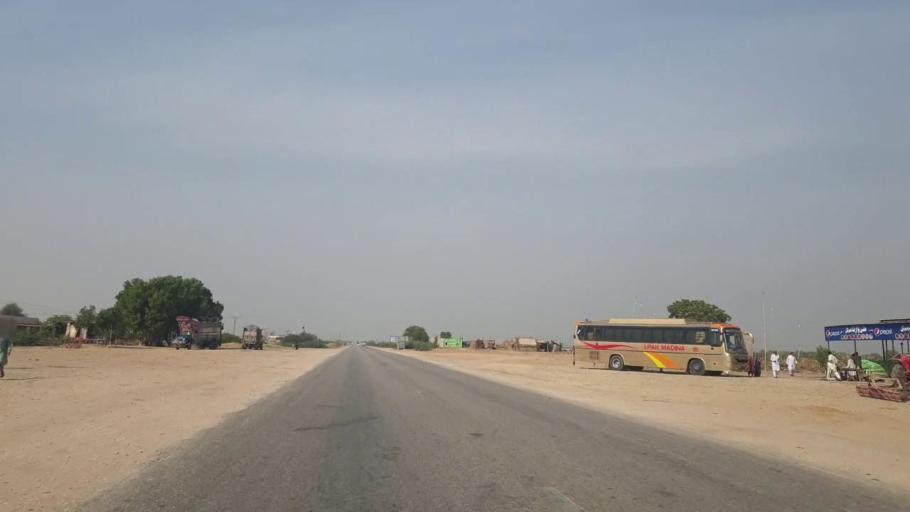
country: PK
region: Sindh
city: Sann
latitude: 26.0584
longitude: 68.1047
